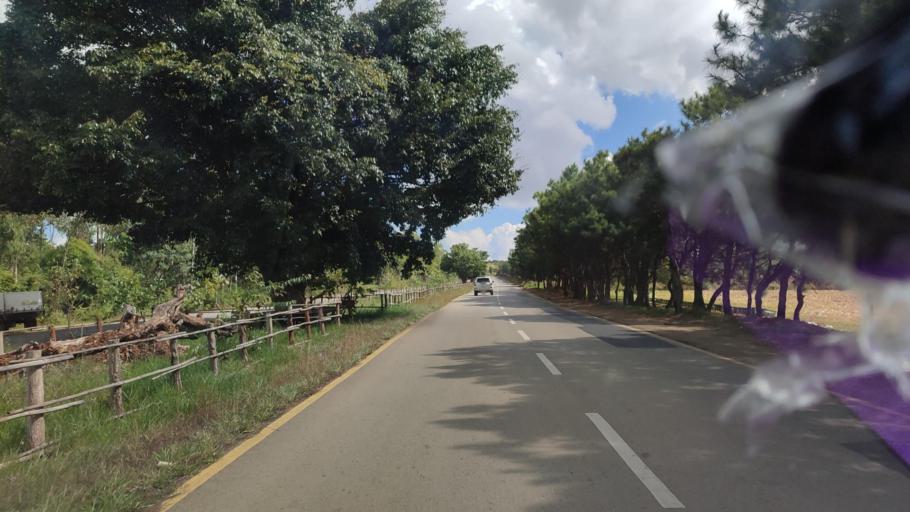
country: MM
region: Shan
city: Taunggyi
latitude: 20.6774
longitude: 96.7077
